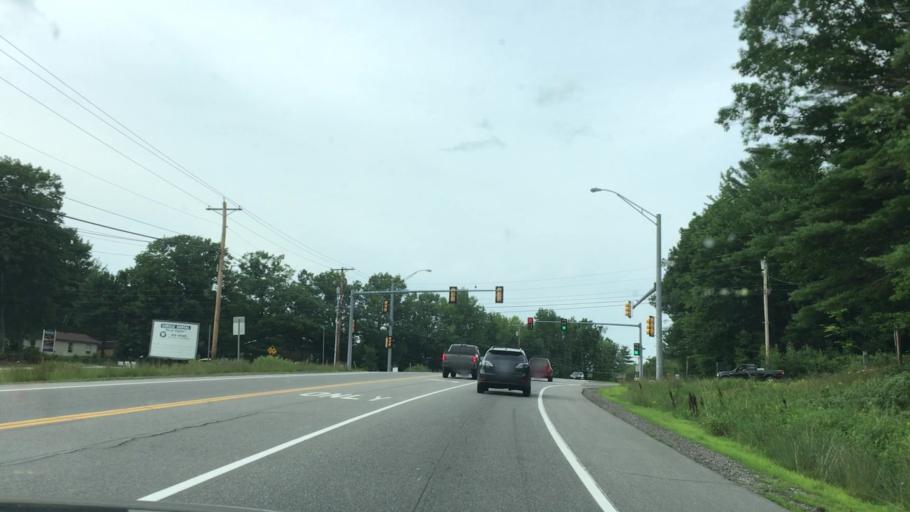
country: US
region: New Hampshire
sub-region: Belknap County
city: Meredith
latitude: 43.6383
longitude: -71.5299
